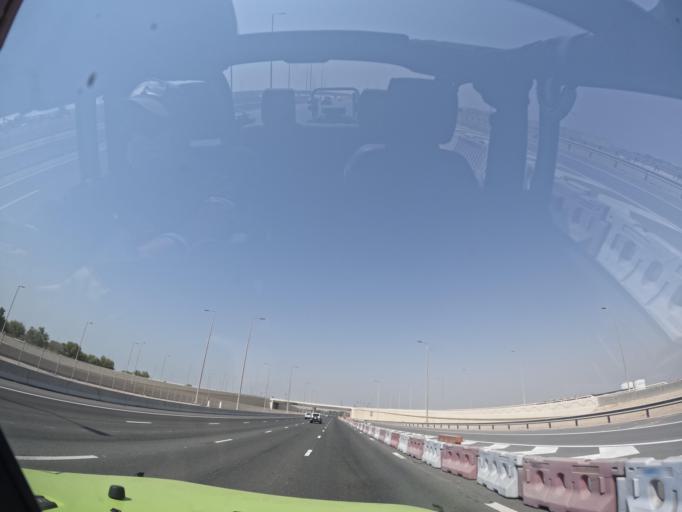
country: AE
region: Abu Dhabi
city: Abu Dhabi
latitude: 24.4613
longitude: 54.6281
